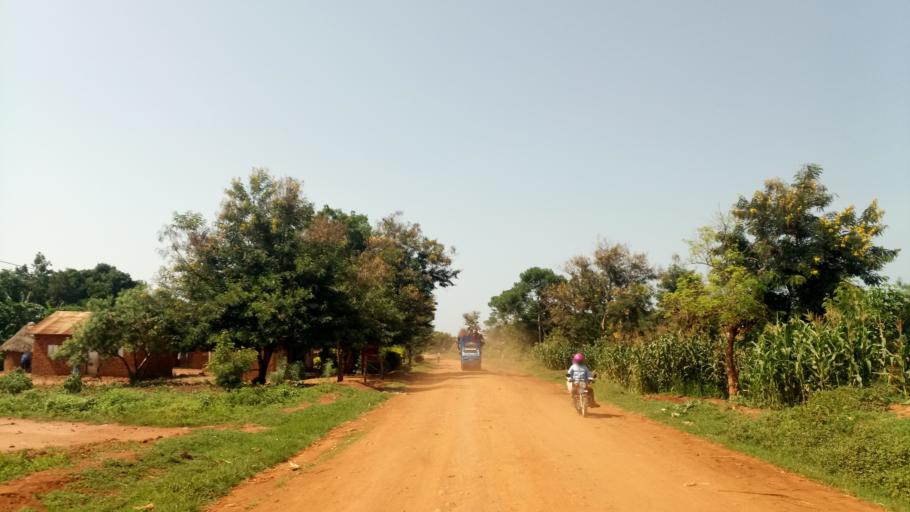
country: UG
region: Eastern Region
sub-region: Kaliro District
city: Kaliro
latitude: 0.9598
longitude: 33.4711
